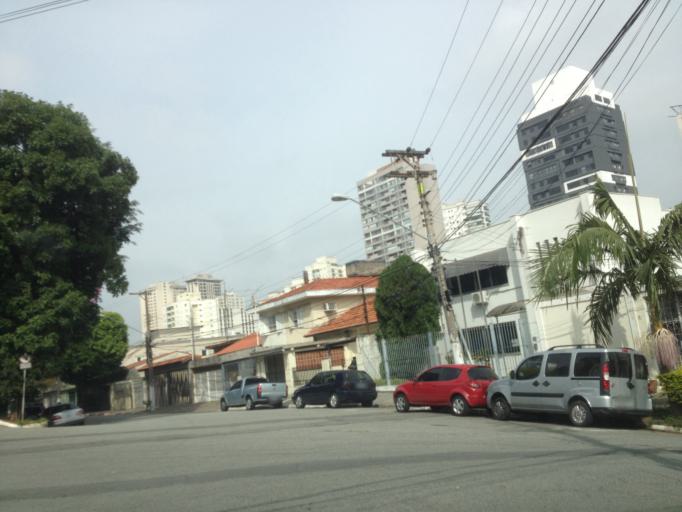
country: BR
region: Sao Paulo
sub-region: Diadema
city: Diadema
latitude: -23.6226
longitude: -46.6658
